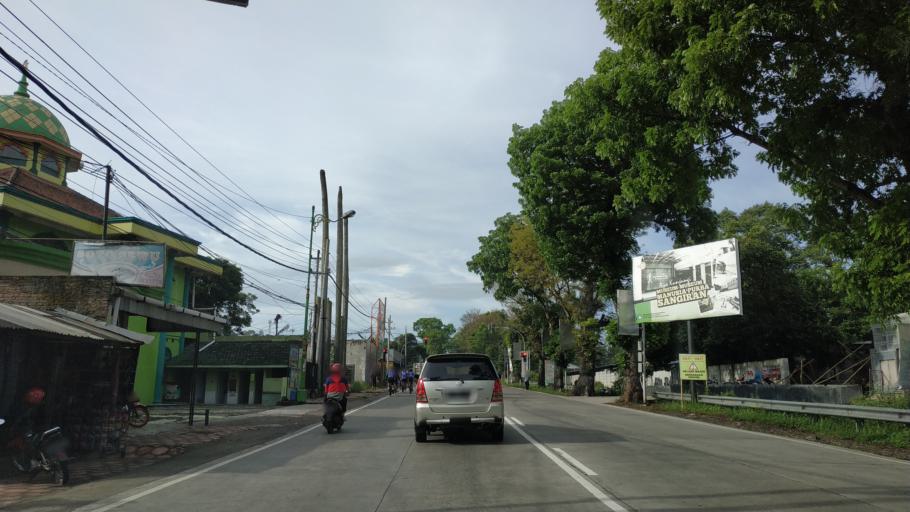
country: ID
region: Central Java
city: Salatiga
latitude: -7.3542
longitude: 110.5127
